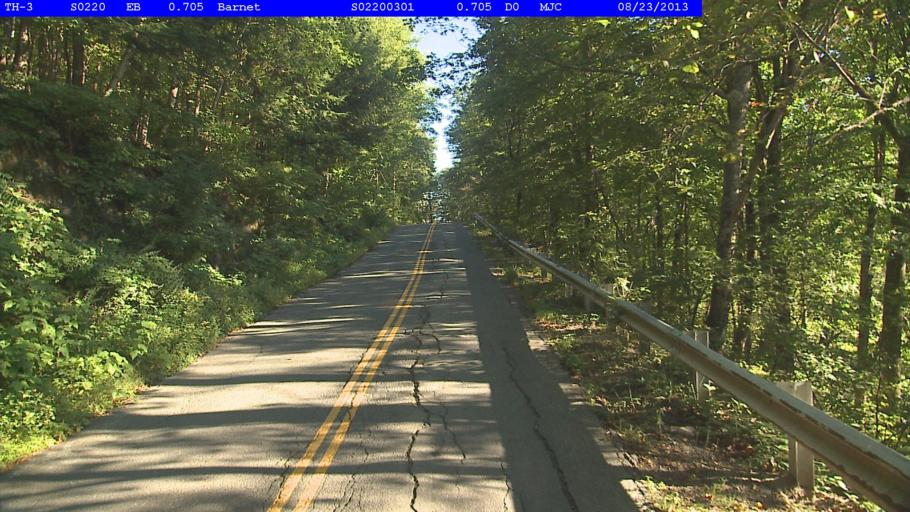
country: US
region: Vermont
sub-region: Caledonia County
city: Saint Johnsbury
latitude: 44.3245
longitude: -72.0332
